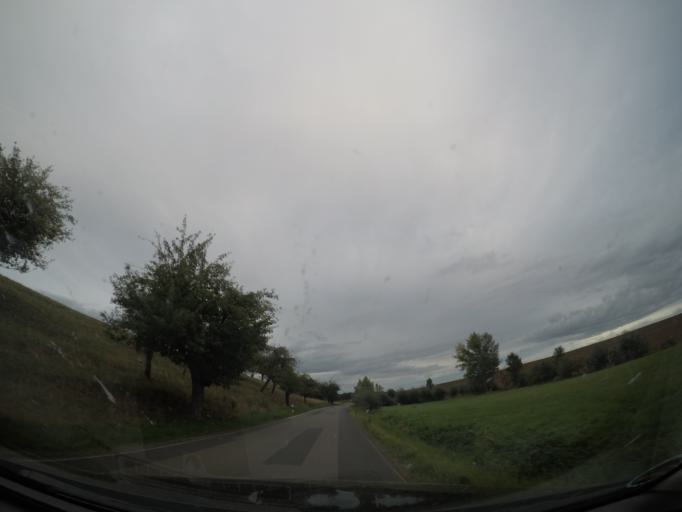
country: DE
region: Thuringia
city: Wildenborten
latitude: 50.9065
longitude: 12.2892
